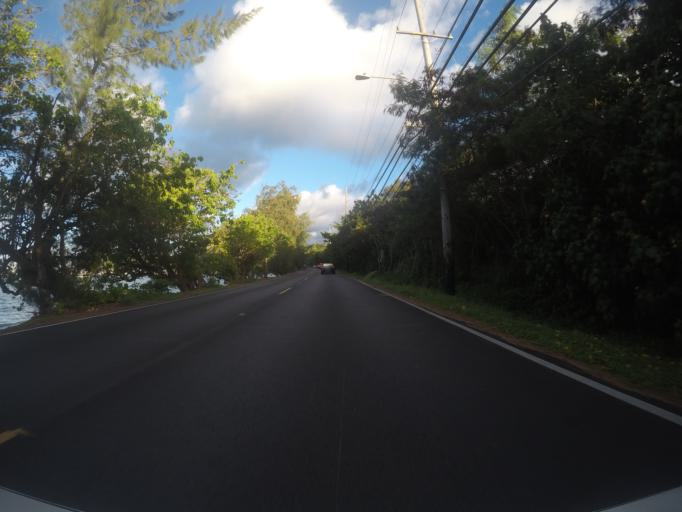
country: US
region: Hawaii
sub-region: Honolulu County
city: He'eia
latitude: 21.4443
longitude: -157.8128
